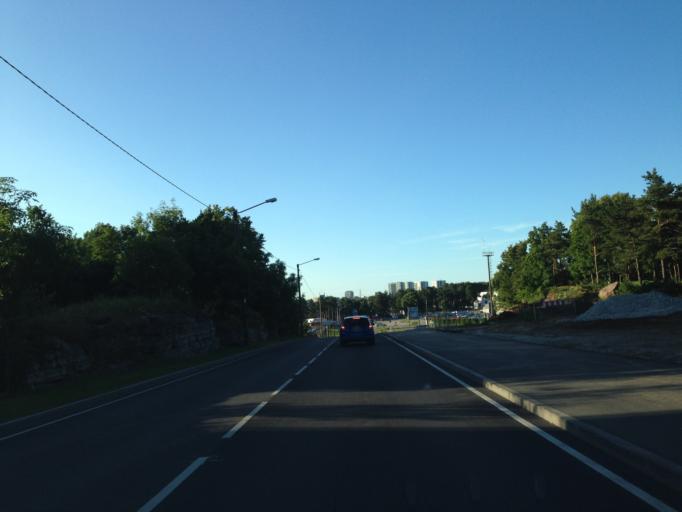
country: EE
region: Harju
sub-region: Saue vald
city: Laagri
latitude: 59.3973
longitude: 24.6452
